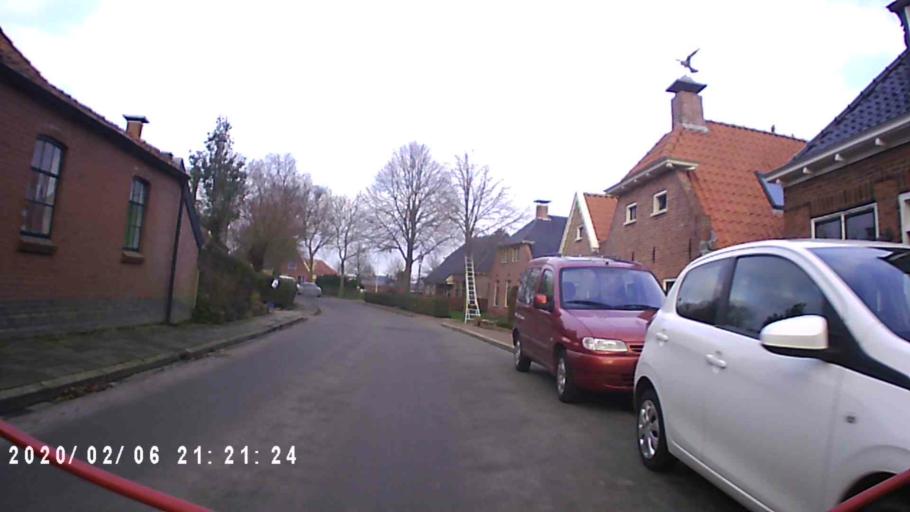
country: NL
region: Groningen
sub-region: Gemeente Zuidhorn
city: Oldehove
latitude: 53.2913
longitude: 6.3675
